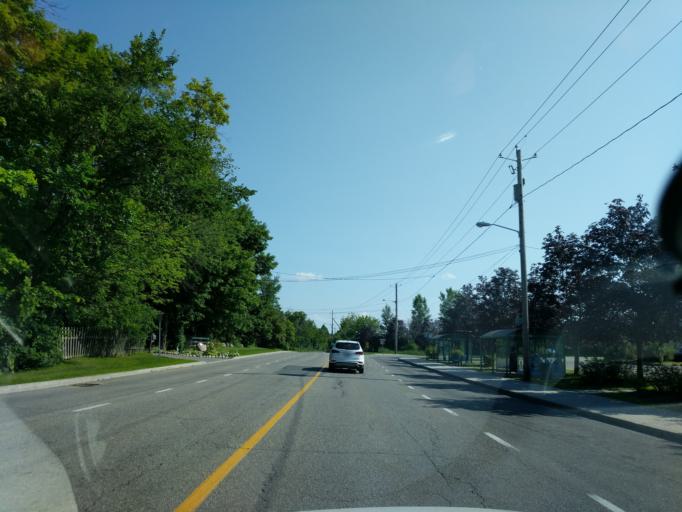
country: CA
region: Ontario
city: Ottawa
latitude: 45.4043
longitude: -75.7935
